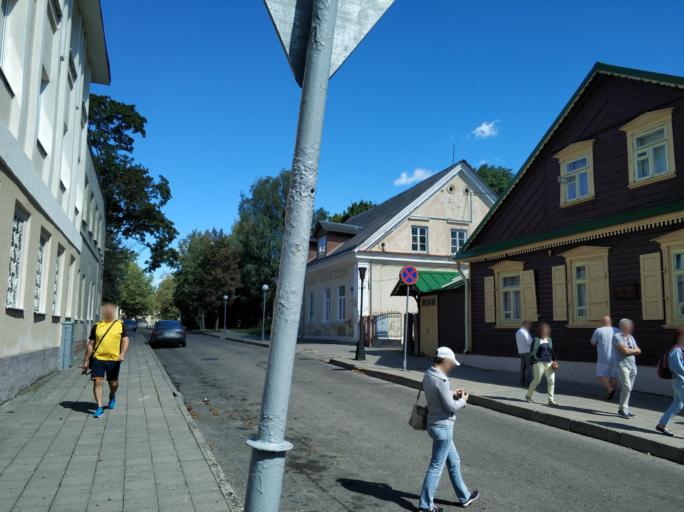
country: BY
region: Grodnenskaya
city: Hrodna
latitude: 53.6872
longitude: 23.8376
